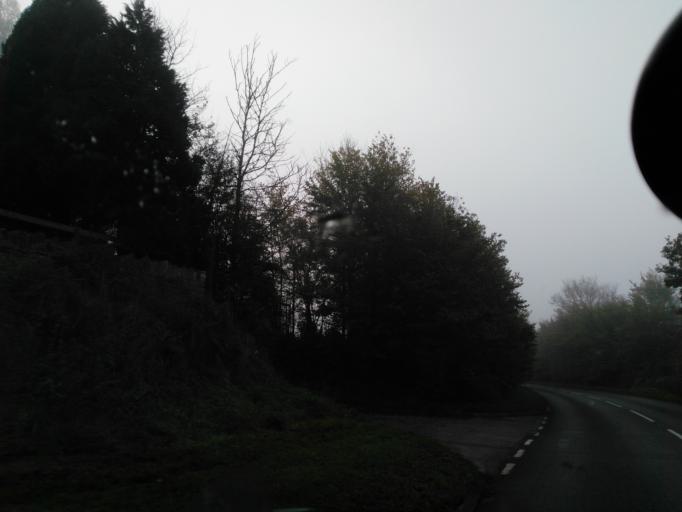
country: GB
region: England
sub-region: Wiltshire
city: Atworth
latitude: 51.4036
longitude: -2.1652
